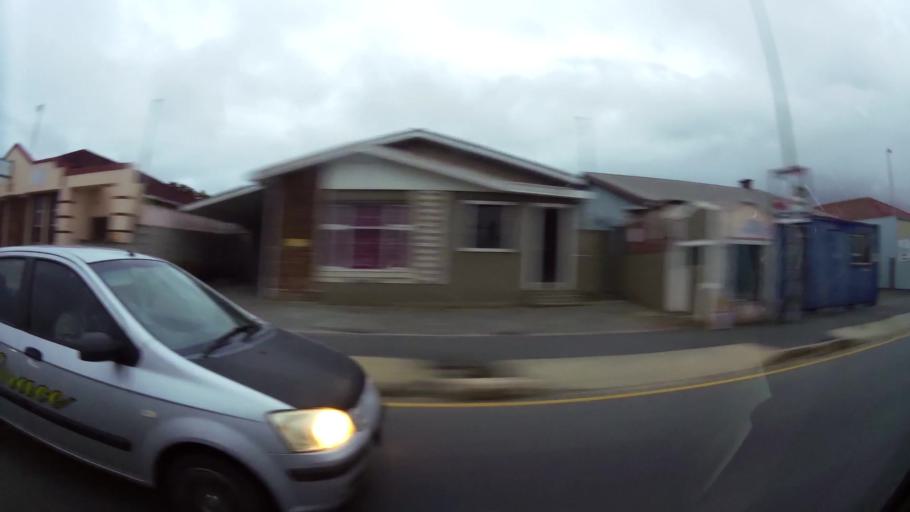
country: ZA
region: Eastern Cape
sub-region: Nelson Mandela Bay Metropolitan Municipality
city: Port Elizabeth
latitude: -33.9275
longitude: 25.5727
